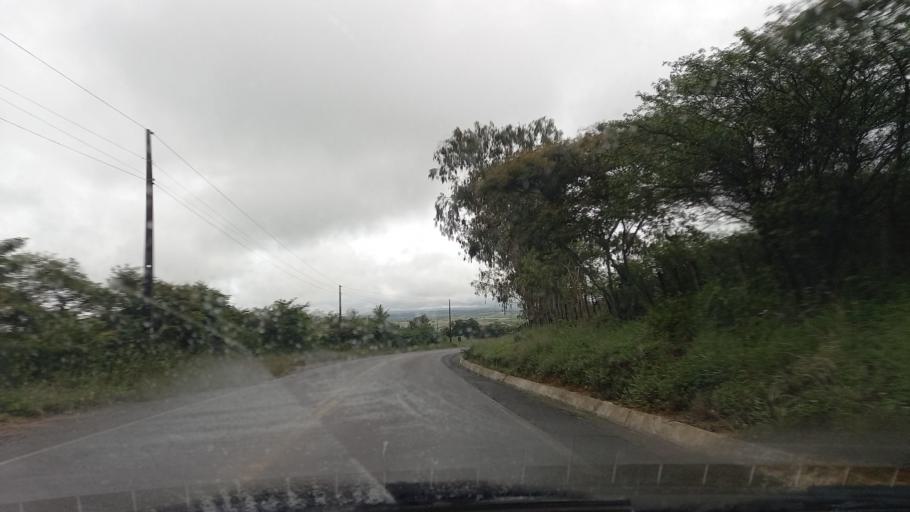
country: BR
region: Pernambuco
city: Garanhuns
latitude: -8.8539
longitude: -36.5144
